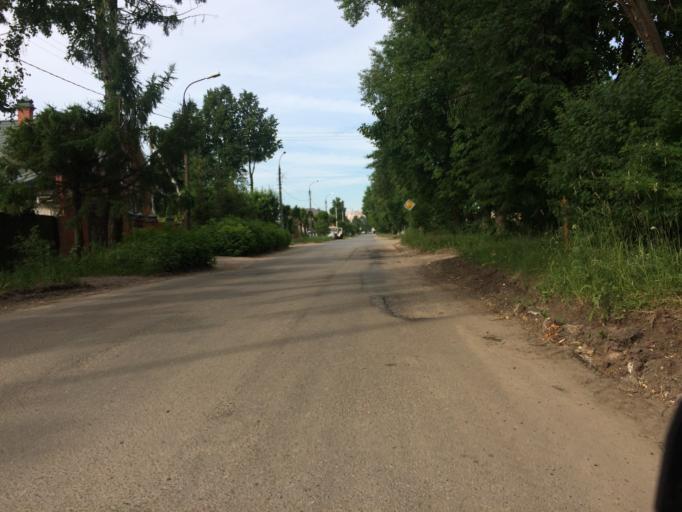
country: RU
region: Mariy-El
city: Yoshkar-Ola
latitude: 56.6492
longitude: 47.9110
